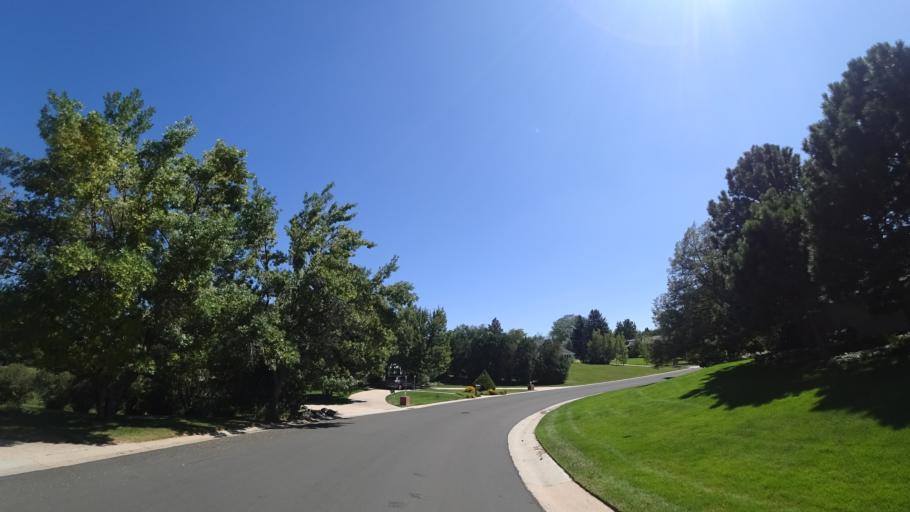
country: US
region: Colorado
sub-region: Arapahoe County
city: Cherry Hills Village
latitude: 39.6333
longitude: -104.9567
